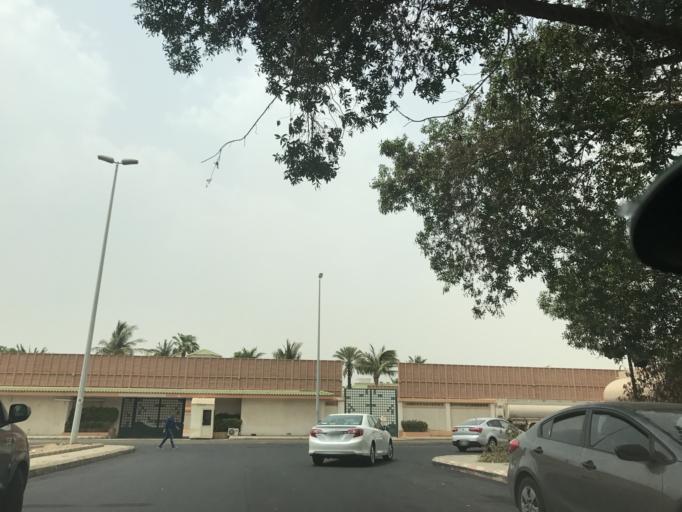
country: SA
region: Makkah
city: Jeddah
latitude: 21.5582
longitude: 39.1693
